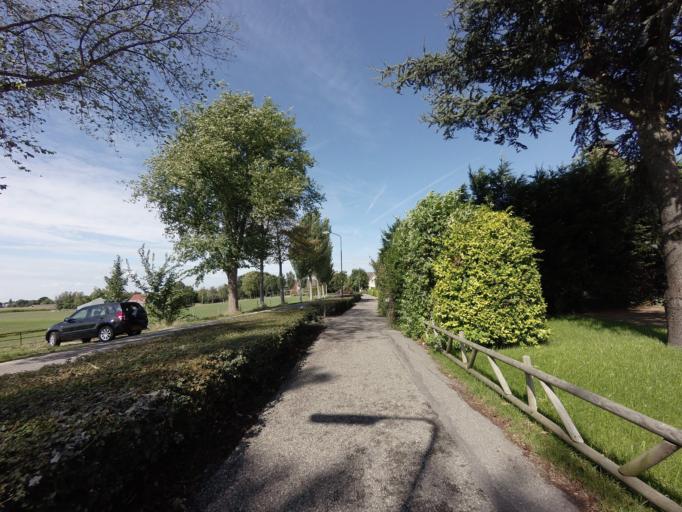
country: NL
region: Utrecht
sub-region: Gemeente De Ronde Venen
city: Mijdrecht
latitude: 52.1981
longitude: 4.8777
